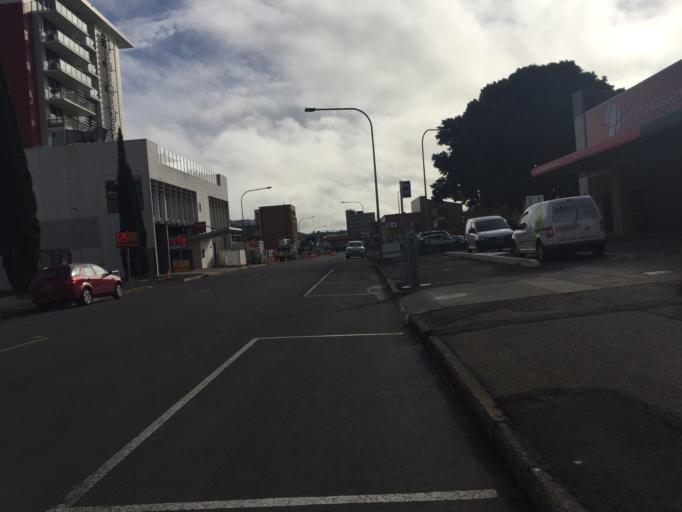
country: AU
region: Queensland
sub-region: Toowoomba
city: Toowoomba
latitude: -27.5642
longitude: 151.9539
